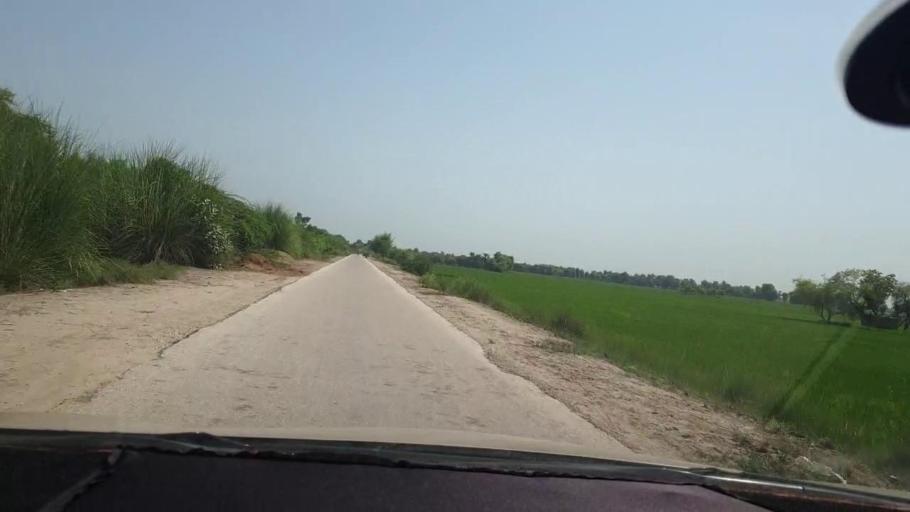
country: PK
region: Sindh
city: Kambar
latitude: 27.5165
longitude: 68.0105
